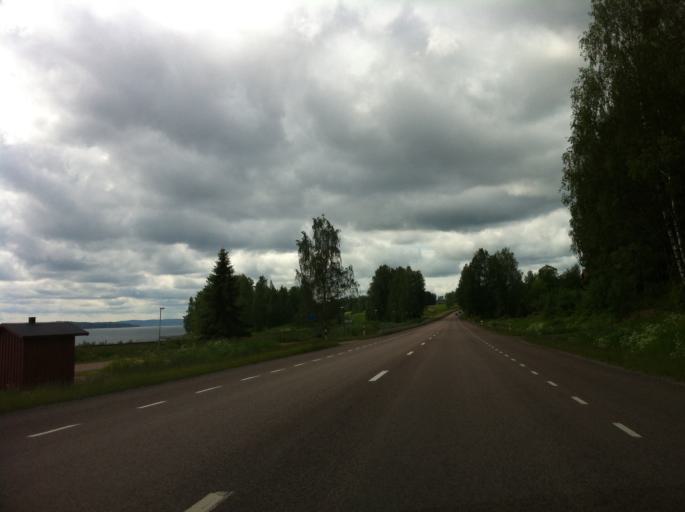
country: SE
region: Vaermland
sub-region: Sunne Kommun
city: Sunne
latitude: 59.8227
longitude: 13.1317
